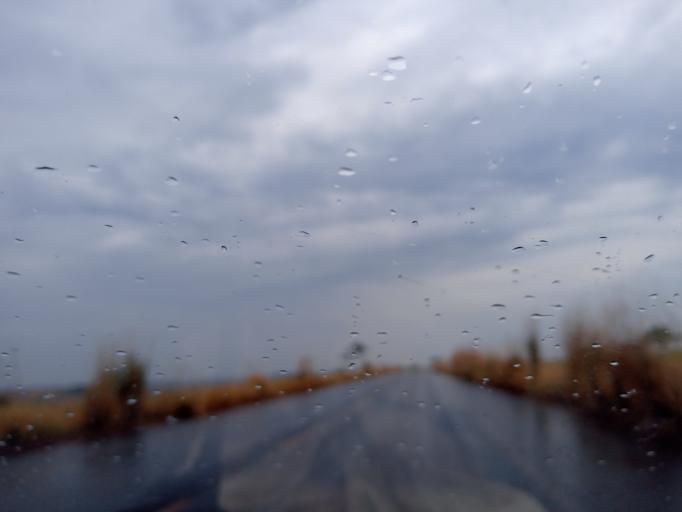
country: BR
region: Minas Gerais
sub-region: Ituiutaba
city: Ituiutaba
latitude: -19.1504
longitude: -49.5263
